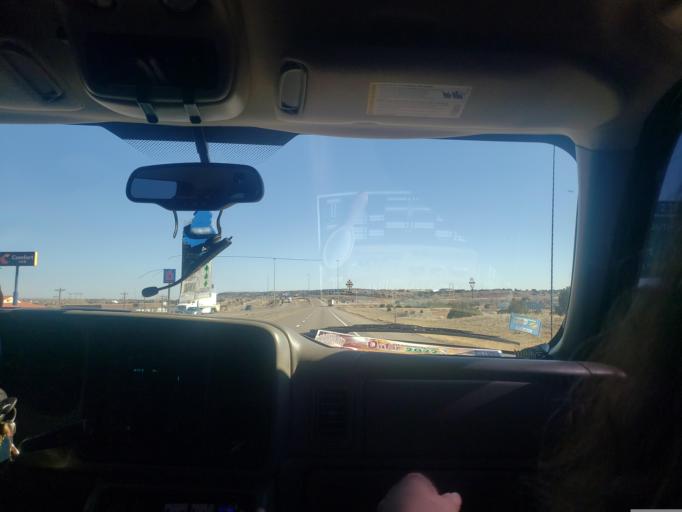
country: US
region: New Mexico
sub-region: Guadalupe County
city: Santa Rosa
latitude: 34.9452
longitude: -104.6480
